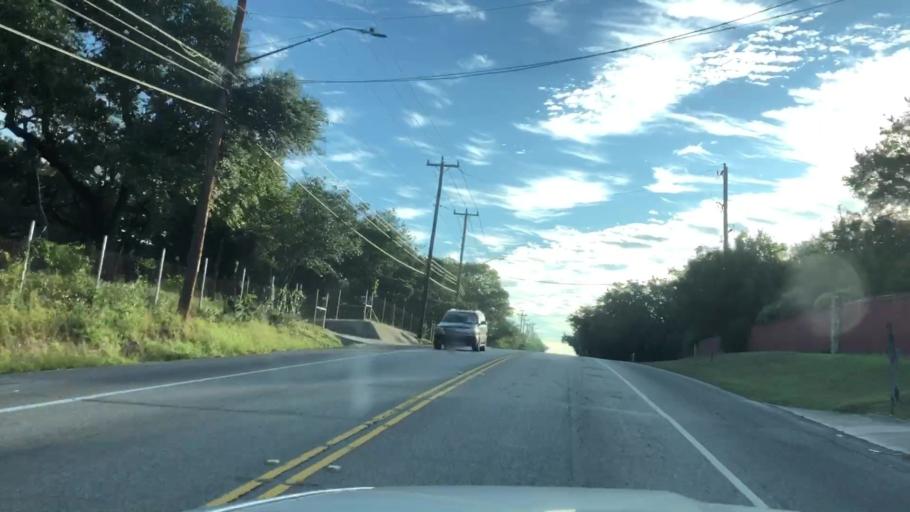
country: US
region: Texas
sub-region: Bexar County
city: Helotes
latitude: 29.5444
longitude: -98.6452
